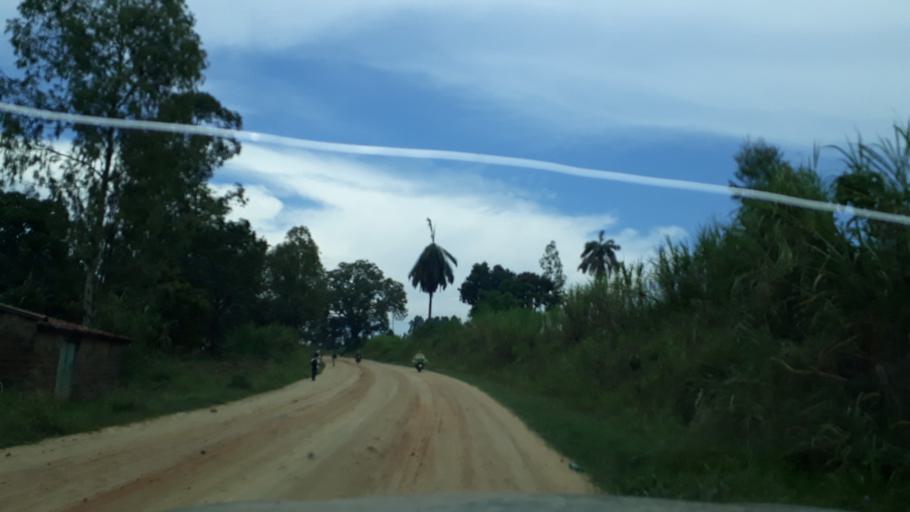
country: CD
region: Eastern Province
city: Bunia
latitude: 1.6509
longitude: 30.2725
